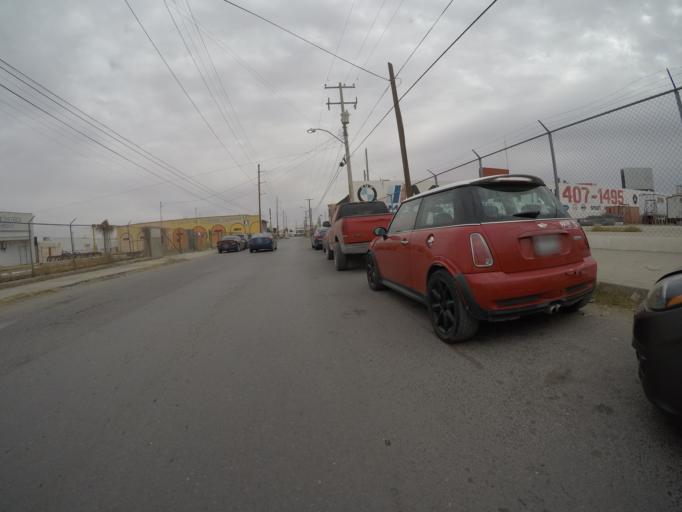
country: MX
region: Chihuahua
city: Ciudad Juarez
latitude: 31.7402
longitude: -106.4276
